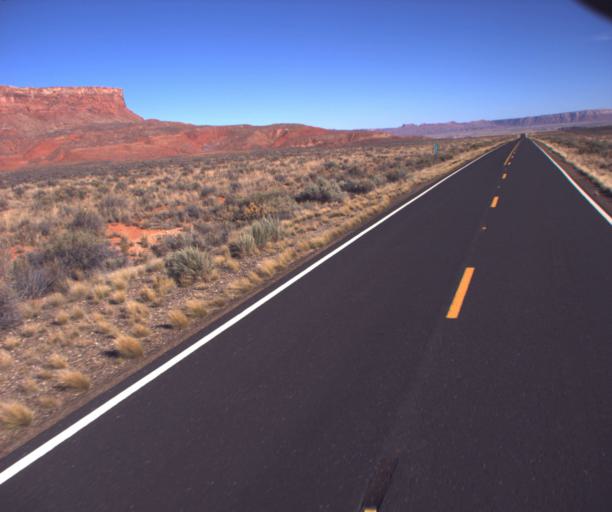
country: US
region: Arizona
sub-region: Coconino County
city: Page
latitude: 36.6936
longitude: -111.8986
